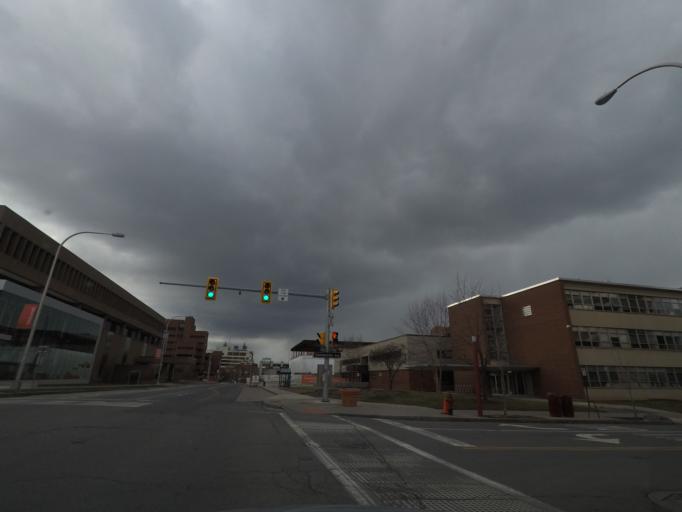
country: US
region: New York
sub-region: Onondaga County
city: Syracuse
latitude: 43.0406
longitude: -76.1344
